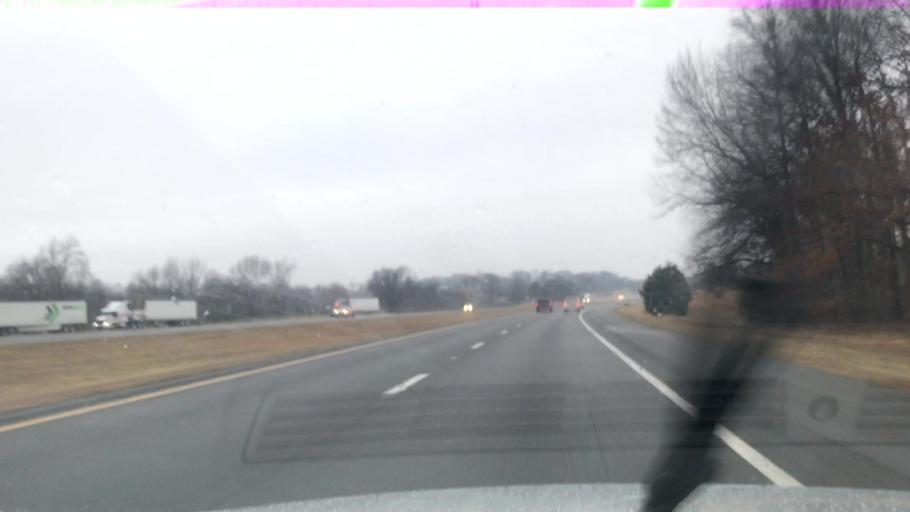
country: US
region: Kentucky
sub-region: Christian County
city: Oak Grove
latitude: 36.6382
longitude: -87.3350
